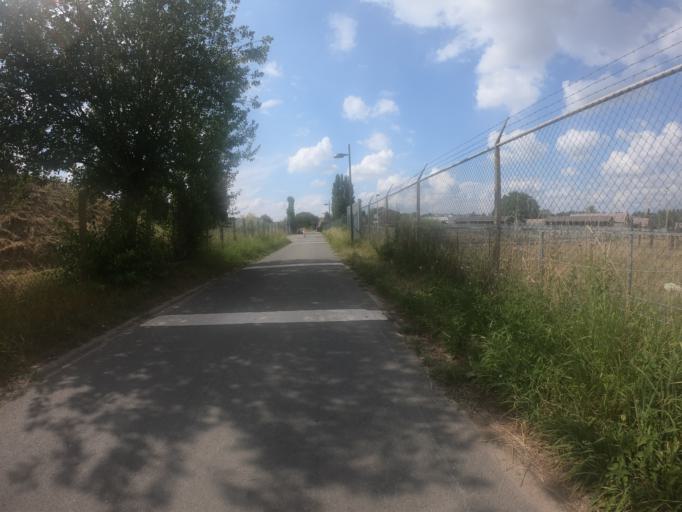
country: BE
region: Flanders
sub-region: Provincie Vlaams-Brabant
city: Dilbeek
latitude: 50.8343
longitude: 4.2677
